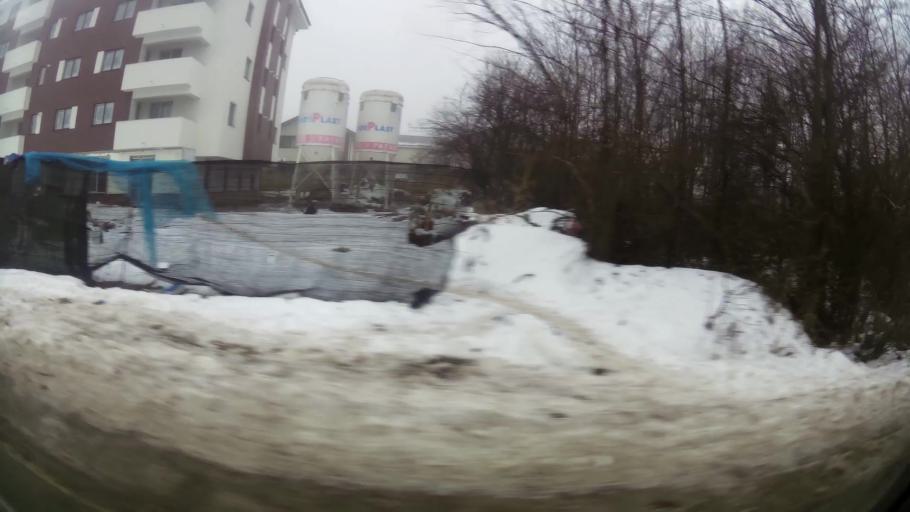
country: RO
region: Ilfov
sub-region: Comuna Chiajna
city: Chiajna
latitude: 44.4588
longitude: 25.9912
